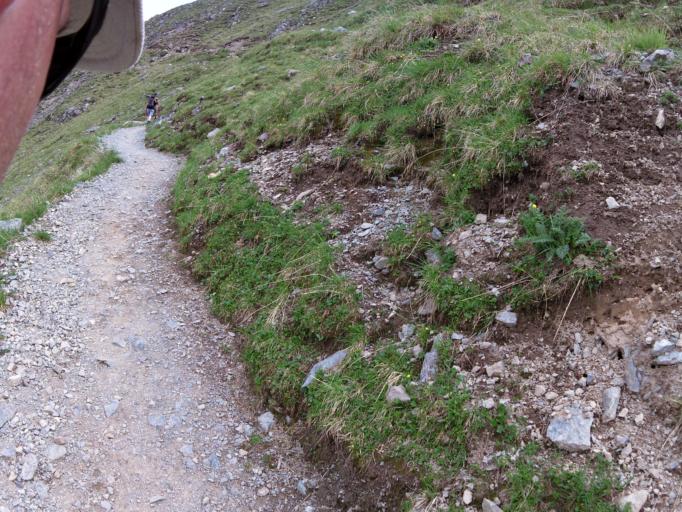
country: AT
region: Tyrol
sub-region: Politischer Bezirk Innsbruck Land
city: Gschnitz
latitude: 47.0447
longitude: 11.3104
